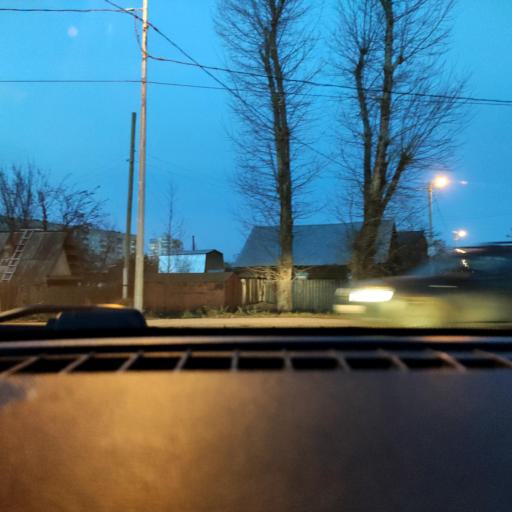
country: RU
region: Perm
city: Kondratovo
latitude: 57.9634
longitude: 56.1562
